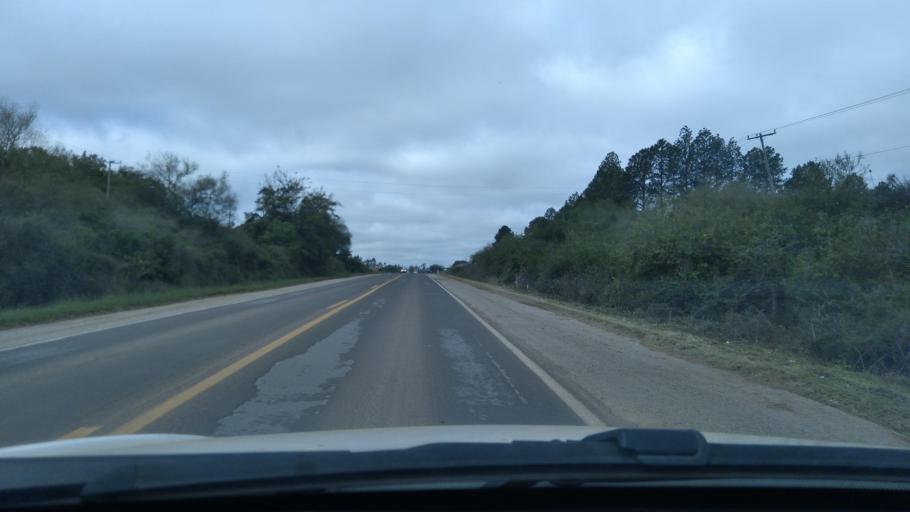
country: BR
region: Rio Grande do Sul
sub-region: Dom Pedrito
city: Dom Pedrito
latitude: -30.9711
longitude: -54.6562
